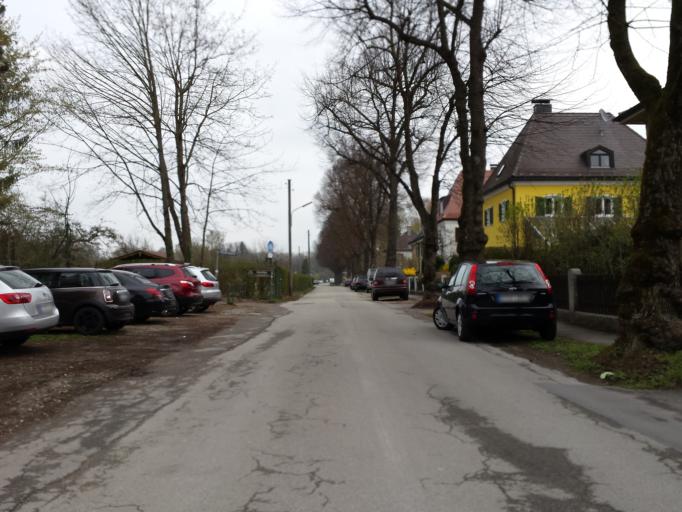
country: DE
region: Bavaria
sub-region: Upper Bavaria
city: Unterfoehring
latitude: 48.1932
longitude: 11.6265
